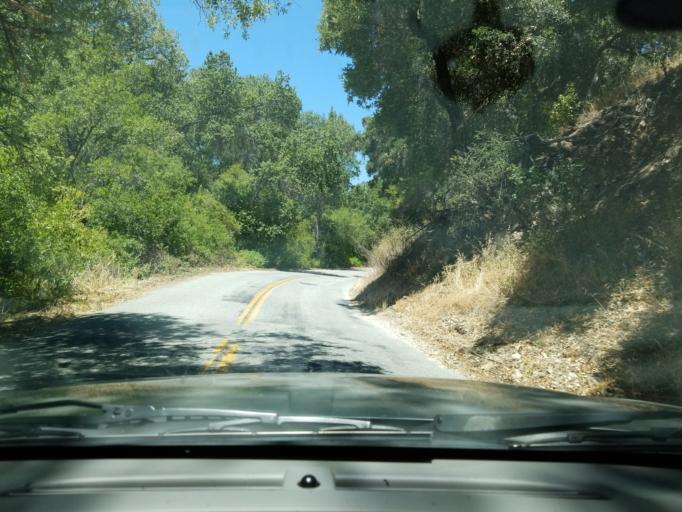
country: US
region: California
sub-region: Monterey County
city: Carmel Valley Village
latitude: 36.4505
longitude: -121.6913
